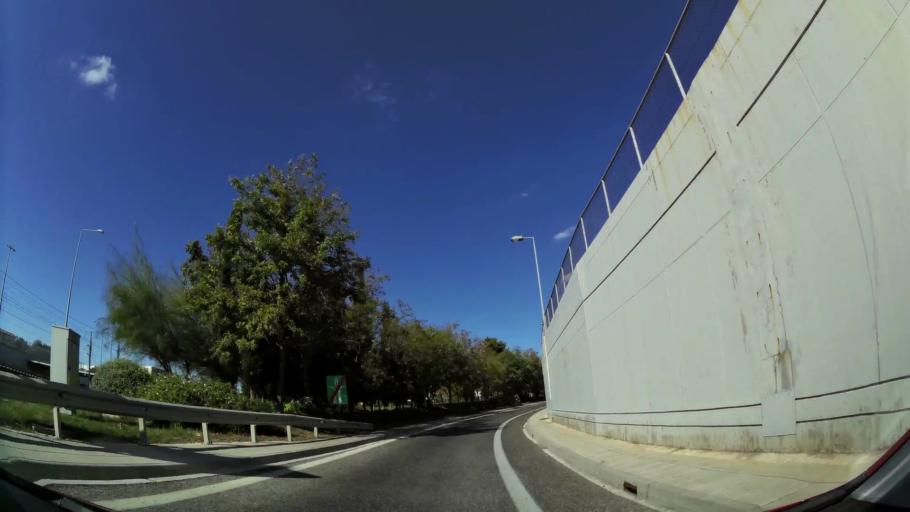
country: GR
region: Attica
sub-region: Nomarchia Anatolikis Attikis
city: Pallini
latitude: 38.0034
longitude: 23.8707
